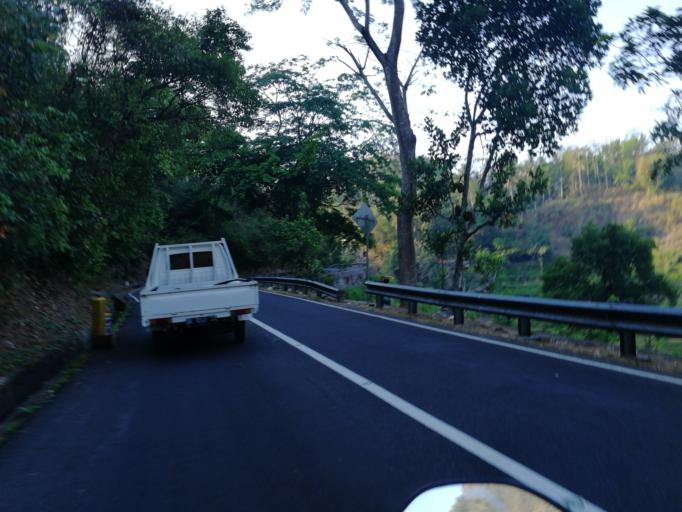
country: ID
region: Bali
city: Tistagede
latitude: -8.3693
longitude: 115.6091
